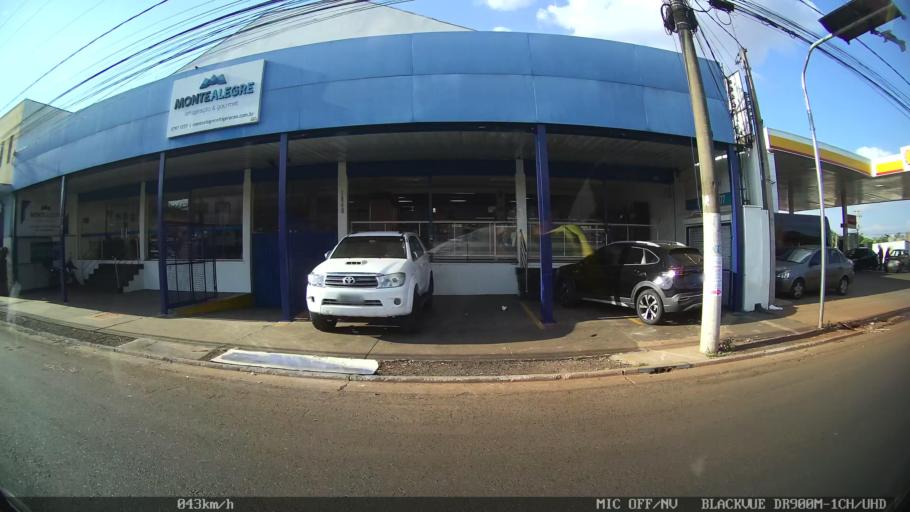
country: BR
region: Sao Paulo
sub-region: Ribeirao Preto
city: Ribeirao Preto
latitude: -21.1490
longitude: -47.8282
